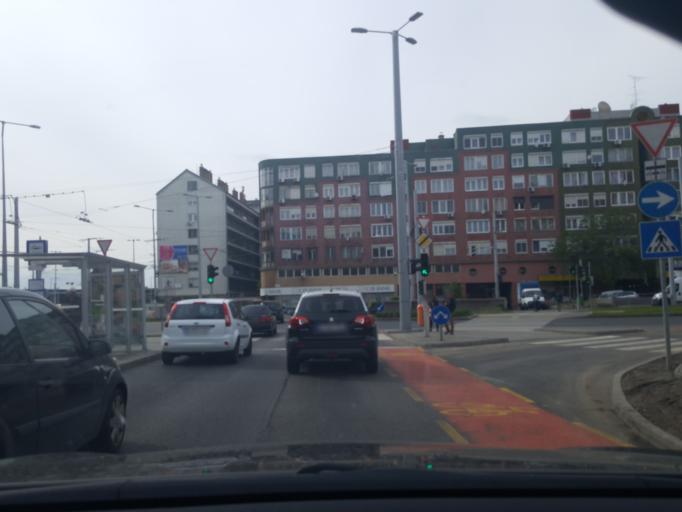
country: HU
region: Budapest
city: Budapest X. keruelet
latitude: 47.4823
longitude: 19.1307
